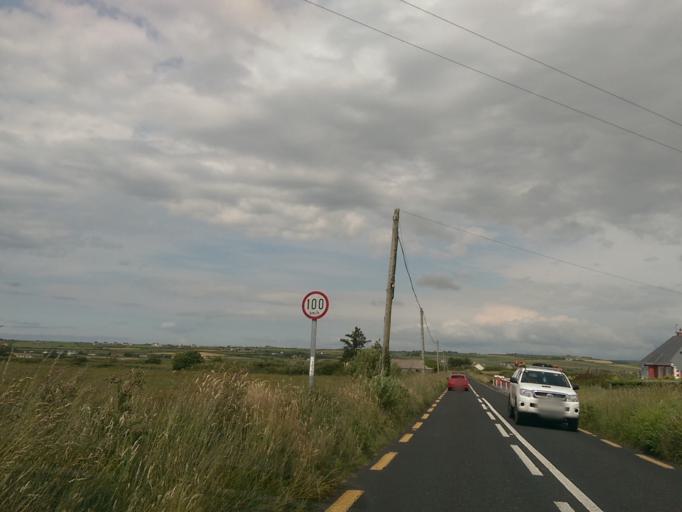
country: IE
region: Munster
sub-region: An Clar
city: Kilrush
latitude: 52.7728
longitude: -9.4457
